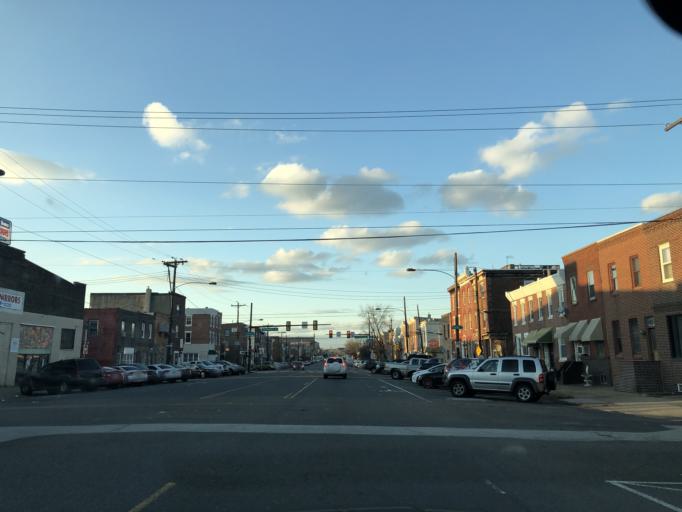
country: US
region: New Jersey
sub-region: Camden County
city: Camden
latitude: 39.9778
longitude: -75.1141
